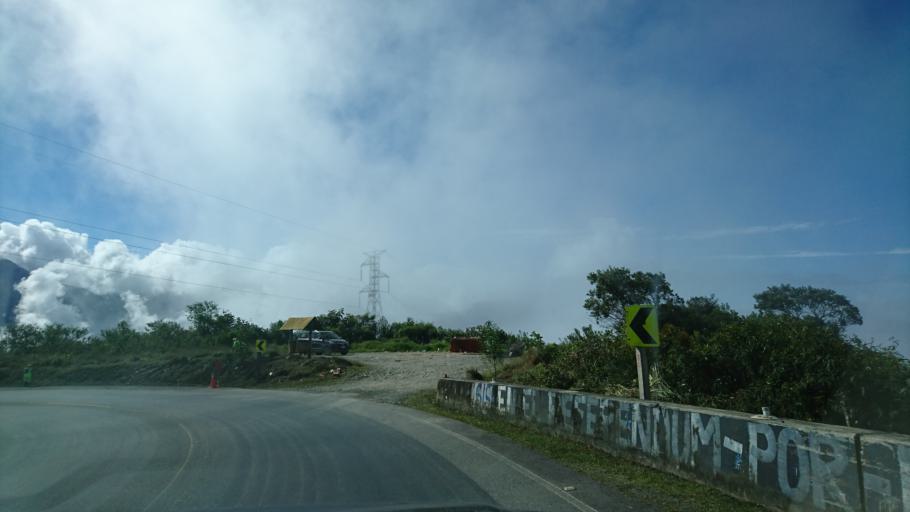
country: BO
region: La Paz
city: Coroico
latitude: -16.2248
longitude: -67.8111
